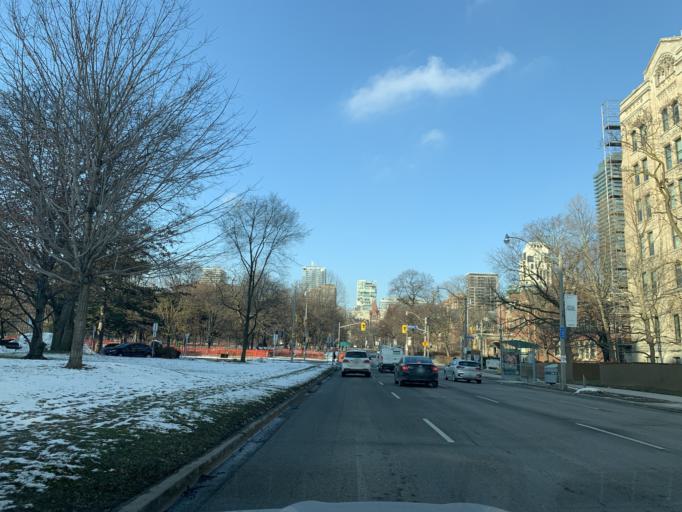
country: CA
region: Ontario
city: Toronto
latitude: 43.6630
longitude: -79.3904
